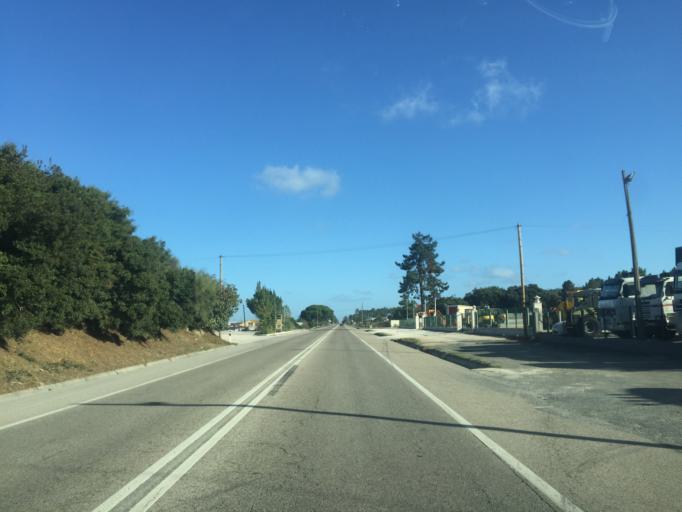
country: PT
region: Leiria
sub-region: Alcobaca
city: Benedita
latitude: 39.4417
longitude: -8.9534
